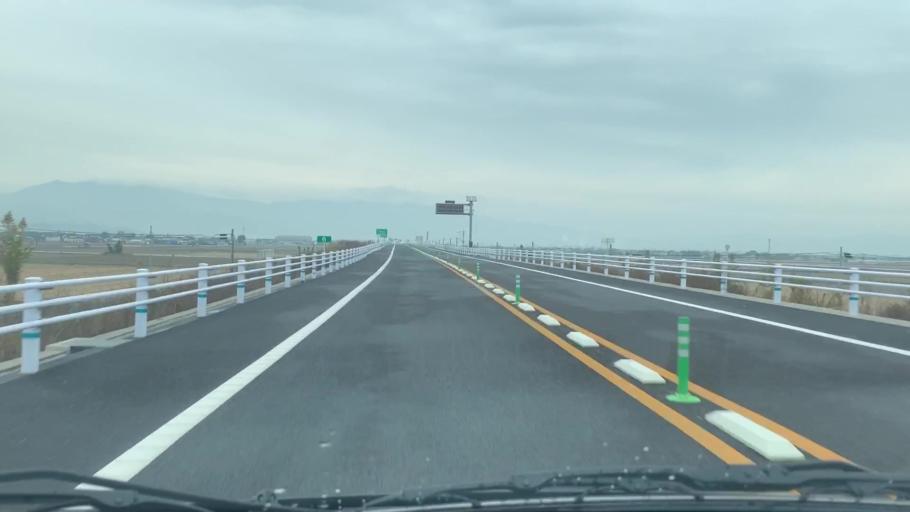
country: JP
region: Saga Prefecture
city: Saga-shi
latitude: 33.2073
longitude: 130.2151
